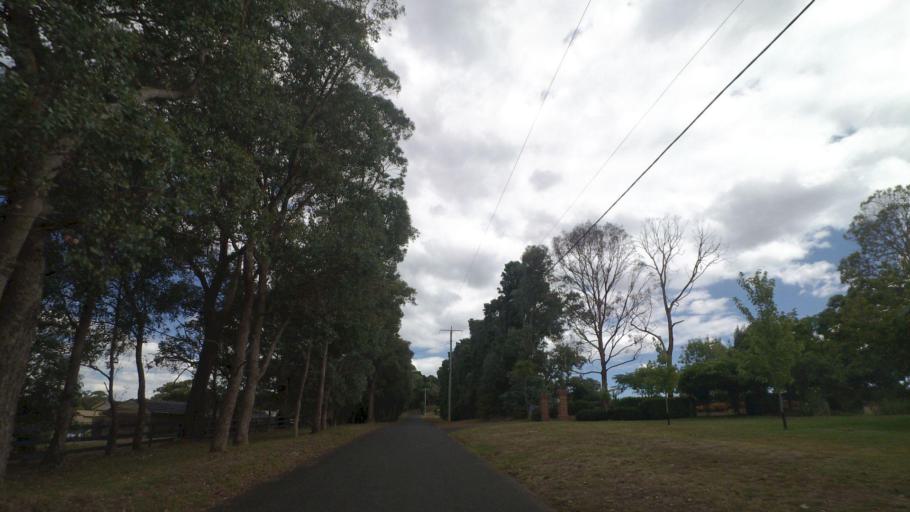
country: AU
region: Victoria
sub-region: Manningham
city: Warrandyte
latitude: -37.7563
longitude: 145.2508
